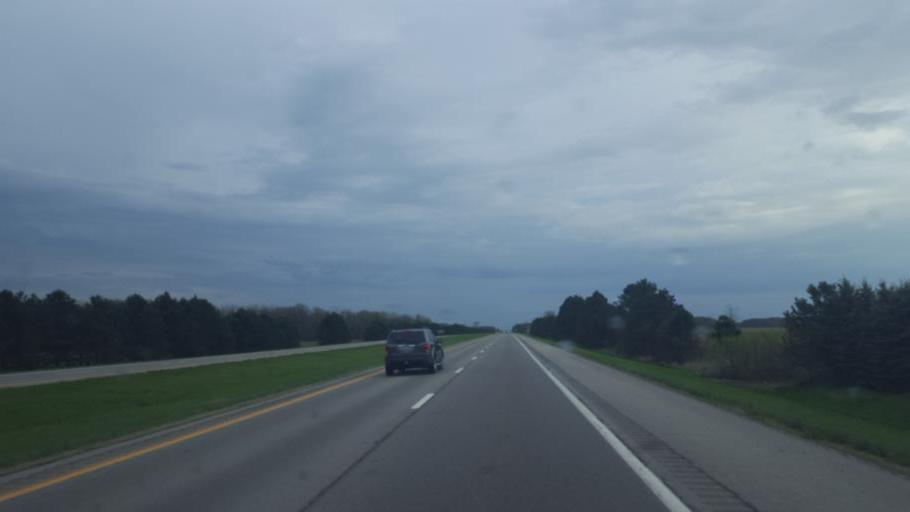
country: US
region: Ohio
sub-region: Wyandot County
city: Carey
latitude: 40.9094
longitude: -83.3501
